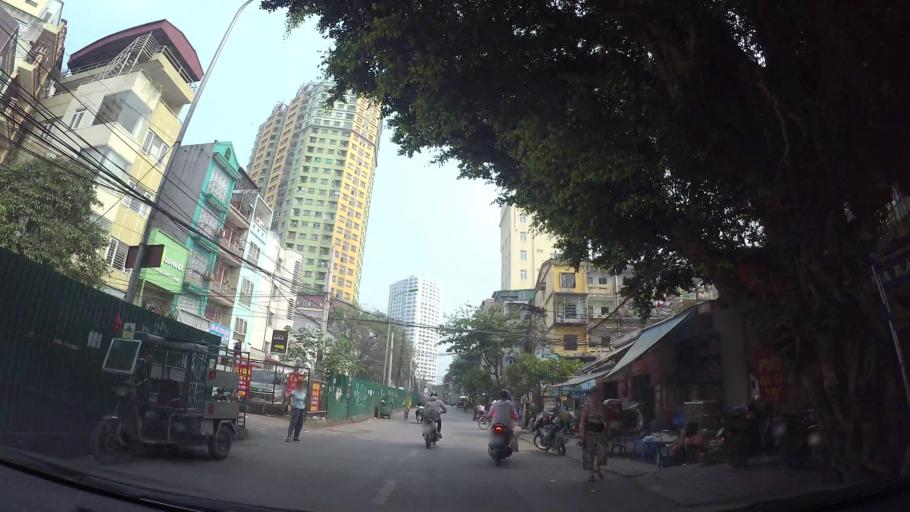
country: VN
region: Ha Noi
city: Cau Giay
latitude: 21.0231
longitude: 105.8118
